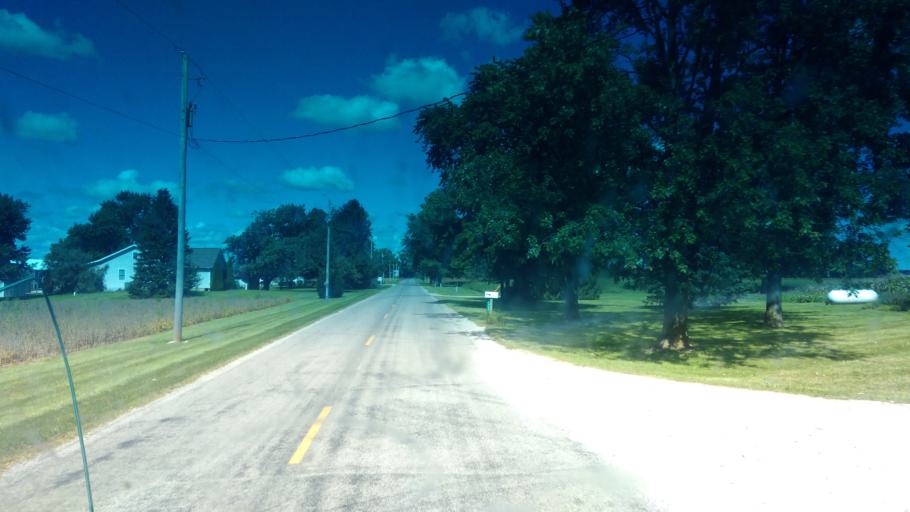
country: US
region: Ohio
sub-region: Madison County
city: Plain City
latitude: 40.0660
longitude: -83.3431
